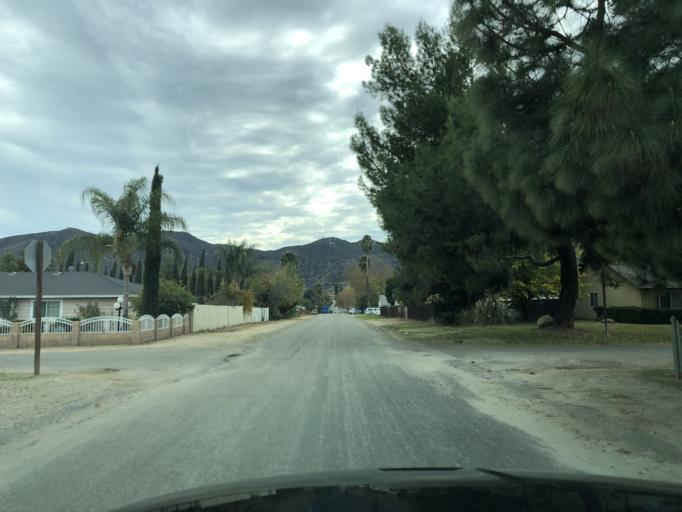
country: US
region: California
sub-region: Riverside County
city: Wildomar
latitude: 33.6043
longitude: -117.2753
